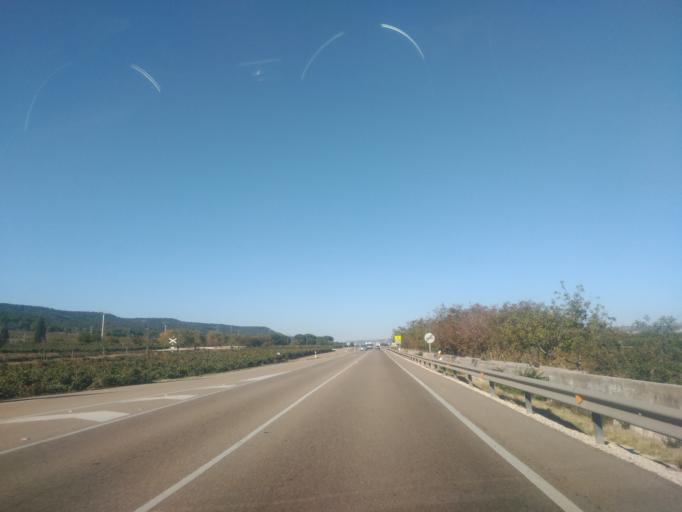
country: ES
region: Castille and Leon
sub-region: Provincia de Valladolid
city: Valbuena de Duero
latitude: 41.6285
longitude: -4.2982
